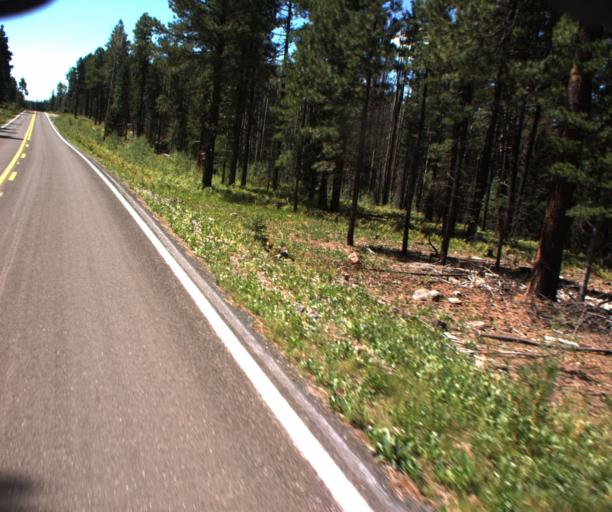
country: US
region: Arizona
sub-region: Apache County
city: Eagar
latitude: 33.6336
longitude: -109.3284
